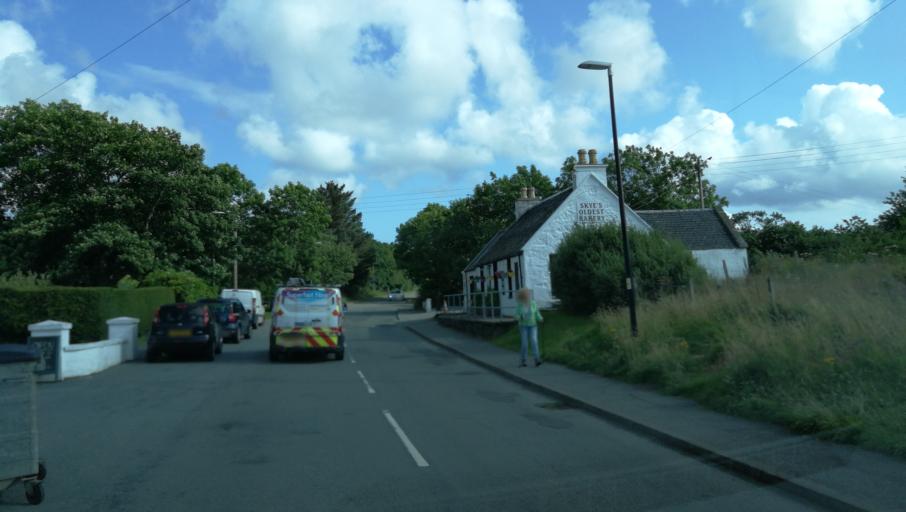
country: GB
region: Scotland
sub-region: Highland
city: Isle of Skye
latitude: 57.4320
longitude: -6.5733
